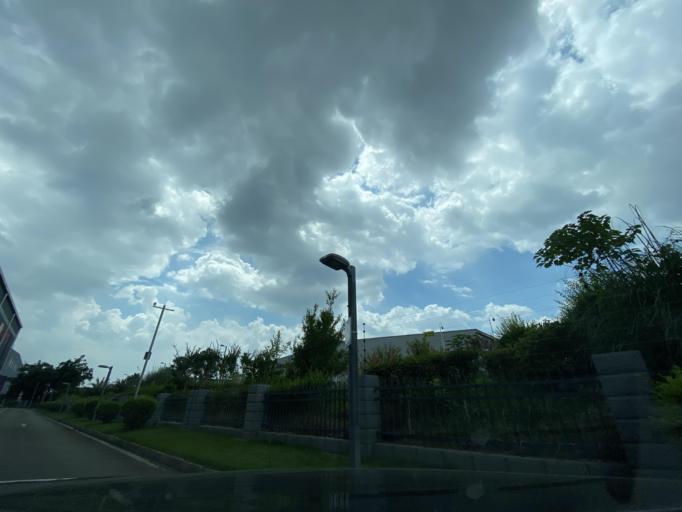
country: CN
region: Sichuan
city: Longquan
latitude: 30.5319
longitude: 104.1952
